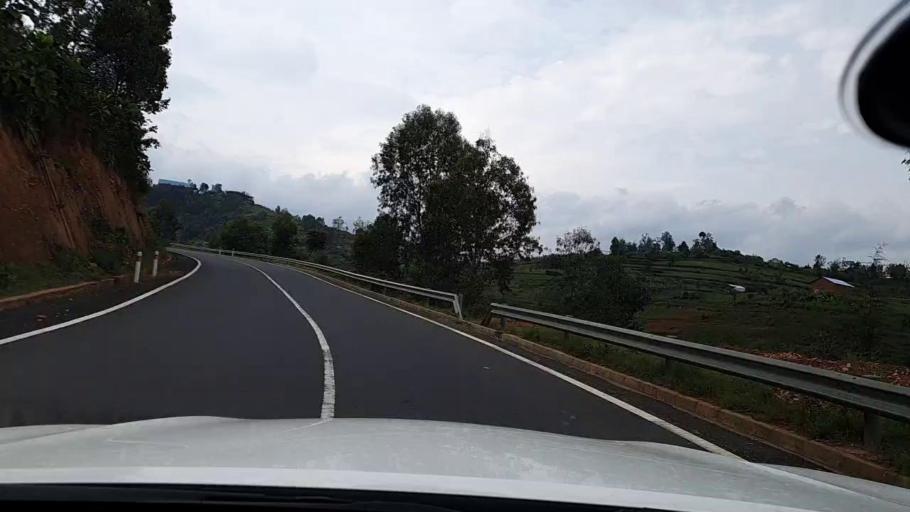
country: RW
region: Western Province
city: Kibuye
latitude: -2.1692
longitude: 29.2893
